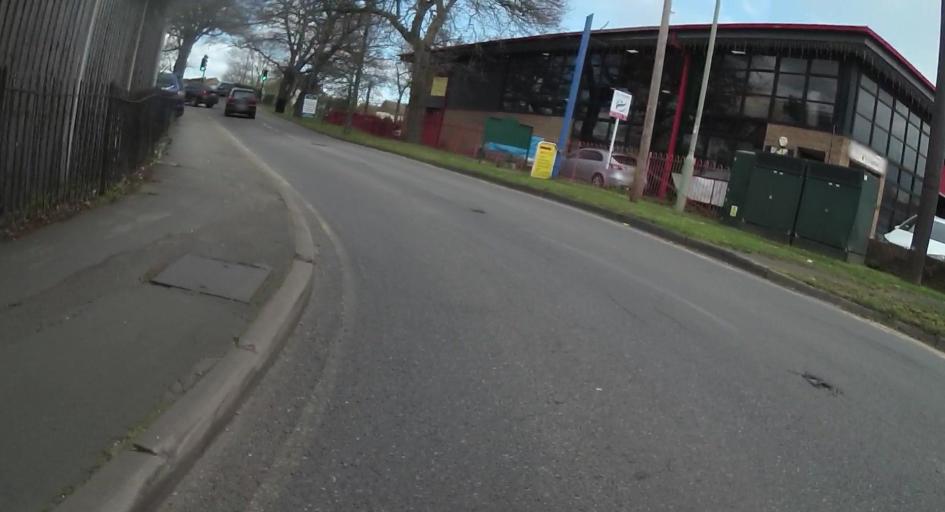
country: GB
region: England
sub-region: Surrey
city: West Byfleet
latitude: 51.3432
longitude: -0.4990
